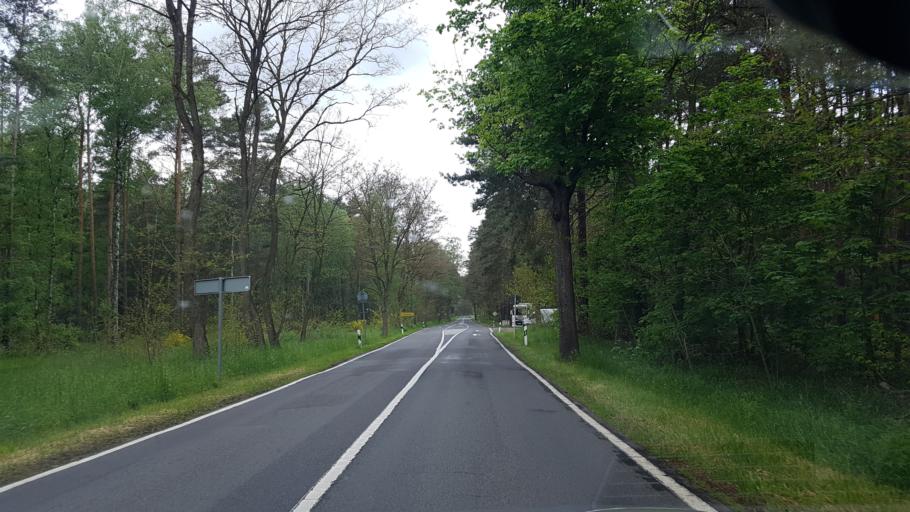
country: DE
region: Brandenburg
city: Jamlitz
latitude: 52.0737
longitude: 14.4039
